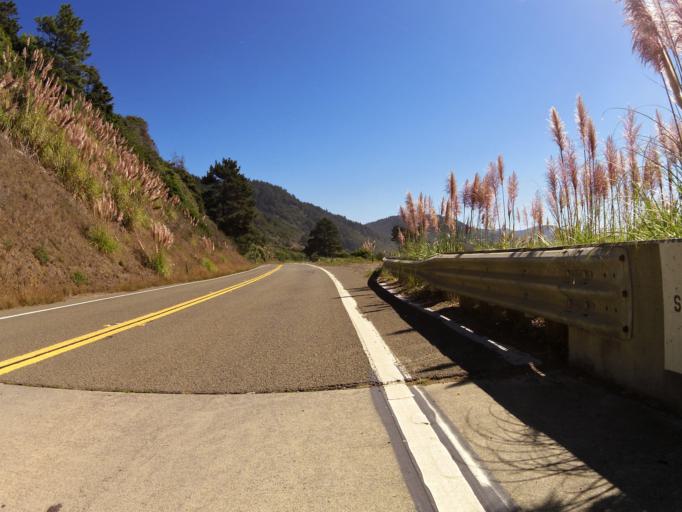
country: US
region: California
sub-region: Mendocino County
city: Fort Bragg
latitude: 39.6934
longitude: -123.7974
